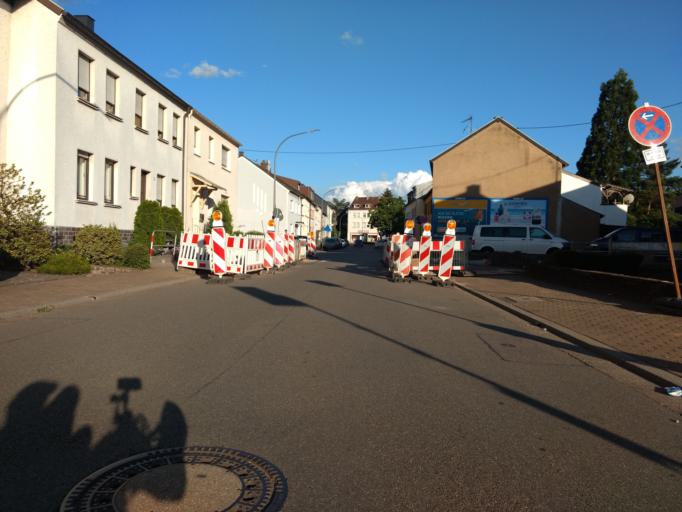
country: DE
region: Saarland
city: Saarlouis
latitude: 49.3271
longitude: 6.7634
